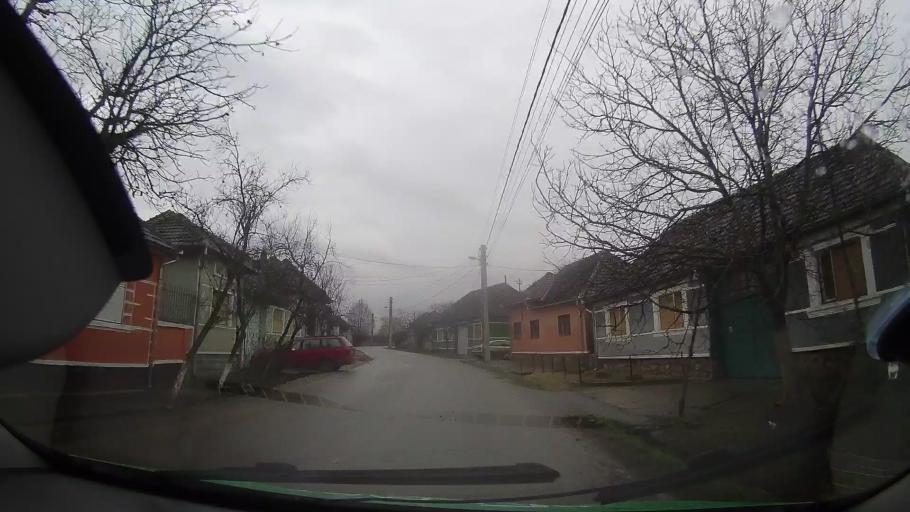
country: RO
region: Bihor
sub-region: Comuna Cociuba Mare
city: Cociuba Mare
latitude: 46.7044
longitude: 22.0486
